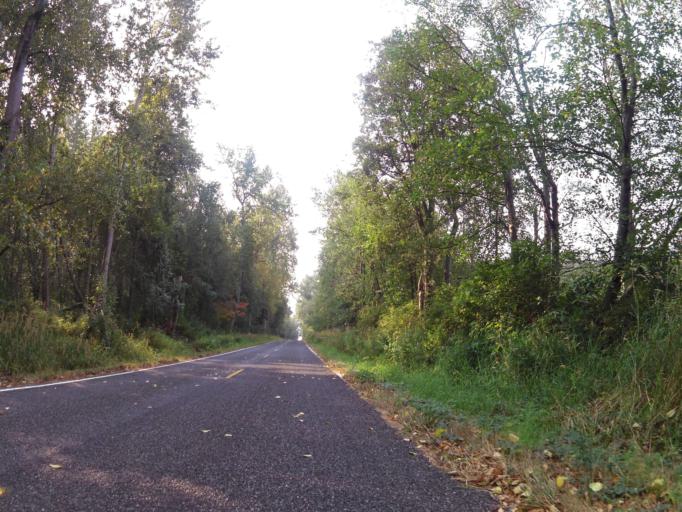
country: US
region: Washington
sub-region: Whatcom County
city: Birch Bay
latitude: 48.8652
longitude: -122.7318
